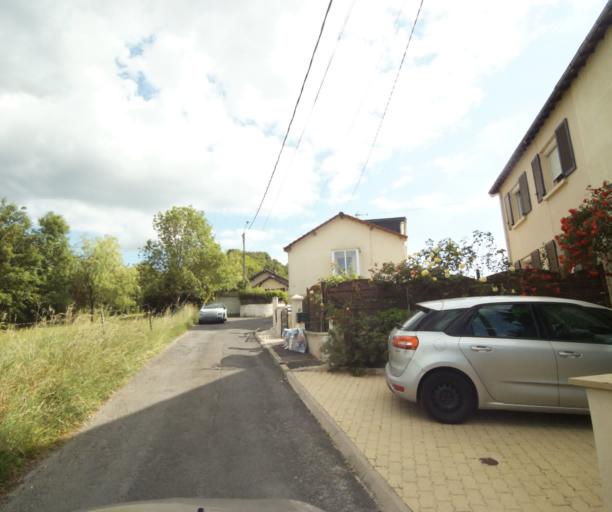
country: FR
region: Champagne-Ardenne
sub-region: Departement des Ardennes
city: Montcy-Notre-Dame
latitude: 49.7719
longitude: 4.7351
